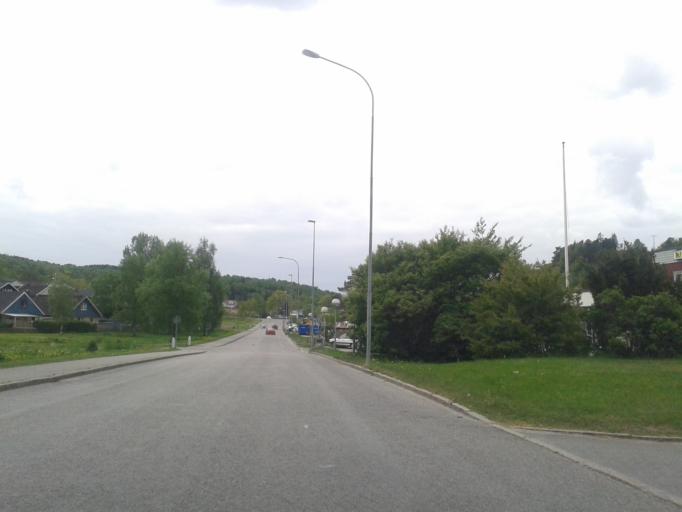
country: SE
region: Vaestra Goetaland
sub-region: Kungalvs Kommun
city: Kungalv
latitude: 57.8731
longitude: 11.9547
